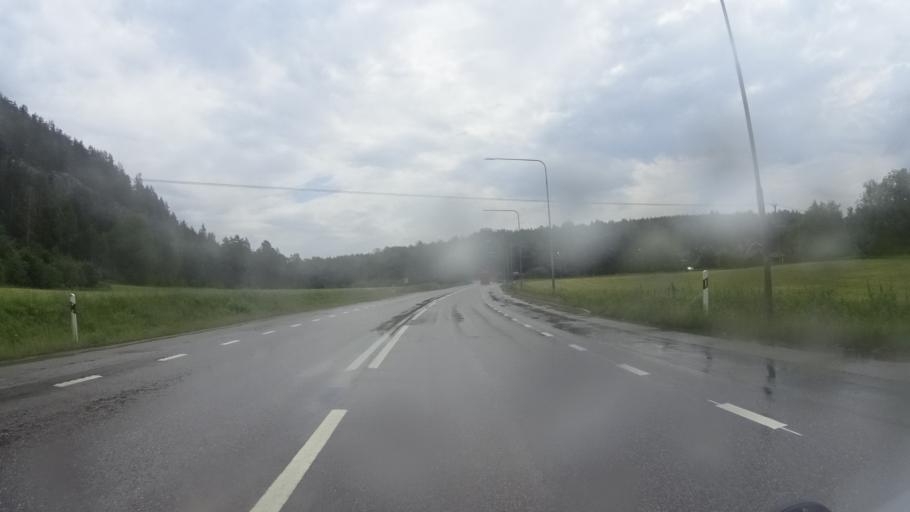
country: SE
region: OEstergoetland
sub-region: Kinda Kommun
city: Kisa
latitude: 57.9778
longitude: 15.6423
